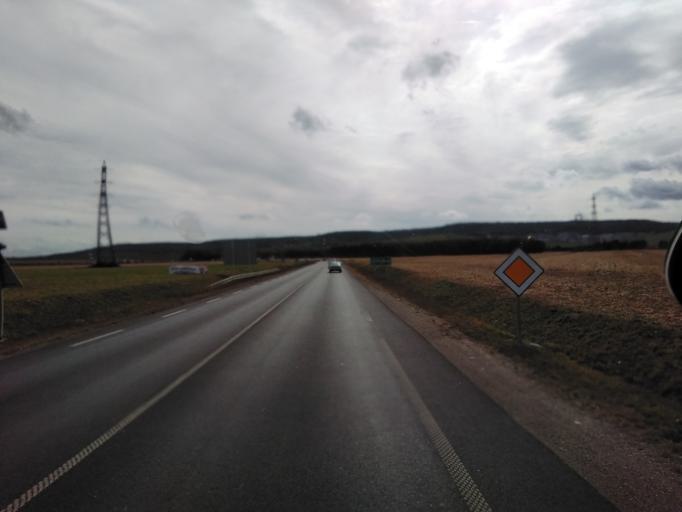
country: FR
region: Champagne-Ardenne
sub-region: Departement de la Marne
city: Verzenay
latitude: 49.1812
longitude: 4.1662
